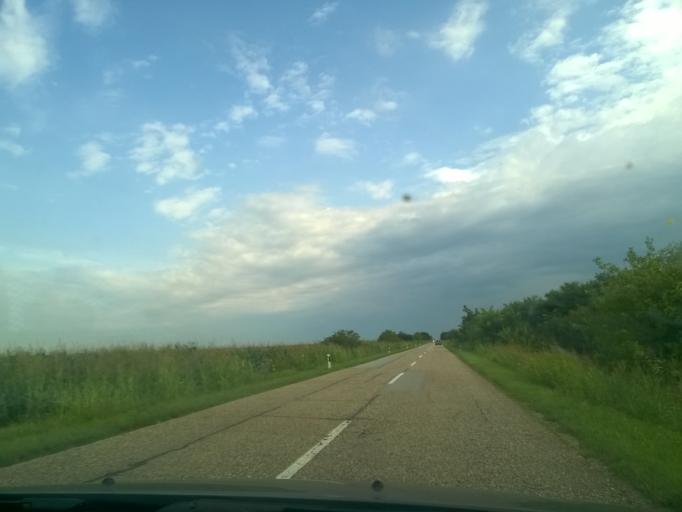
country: RS
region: Autonomna Pokrajina Vojvodina
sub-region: Juznobanatski Okrug
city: Kovacica
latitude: 45.1476
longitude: 20.6167
